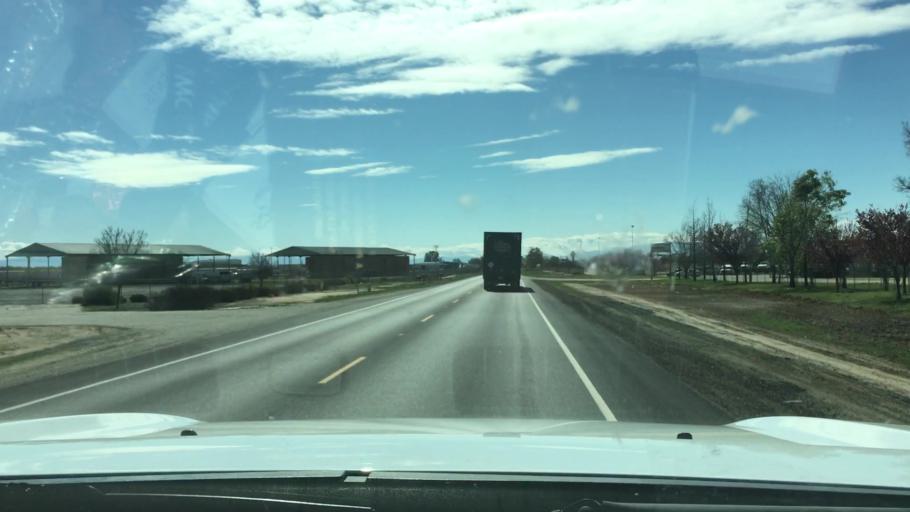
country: US
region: California
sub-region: Kern County
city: Shafter
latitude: 35.4544
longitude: -119.2589
